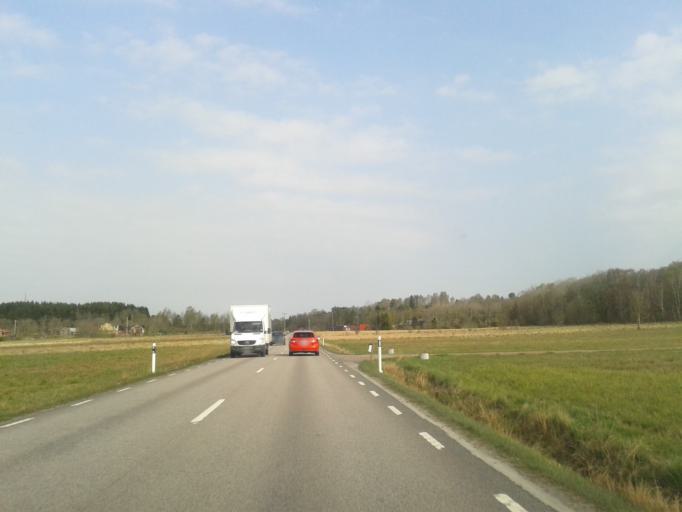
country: SE
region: Vaestra Goetaland
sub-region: Kungalvs Kommun
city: Kode
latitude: 57.8823
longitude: 11.8931
